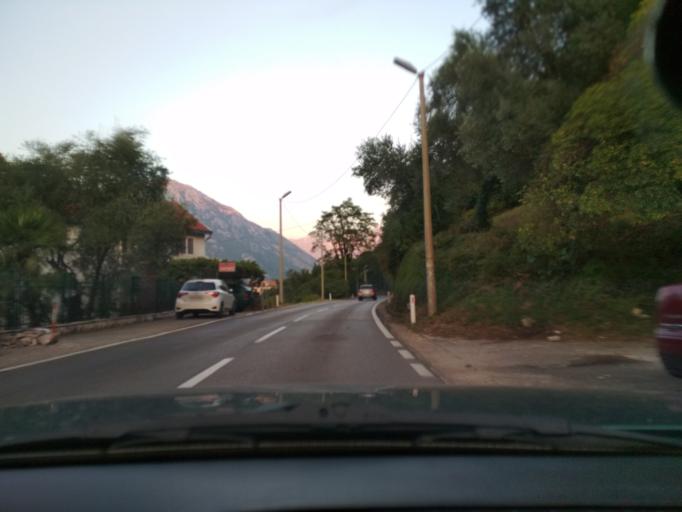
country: ME
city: Lipci
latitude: 42.4871
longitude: 18.6542
